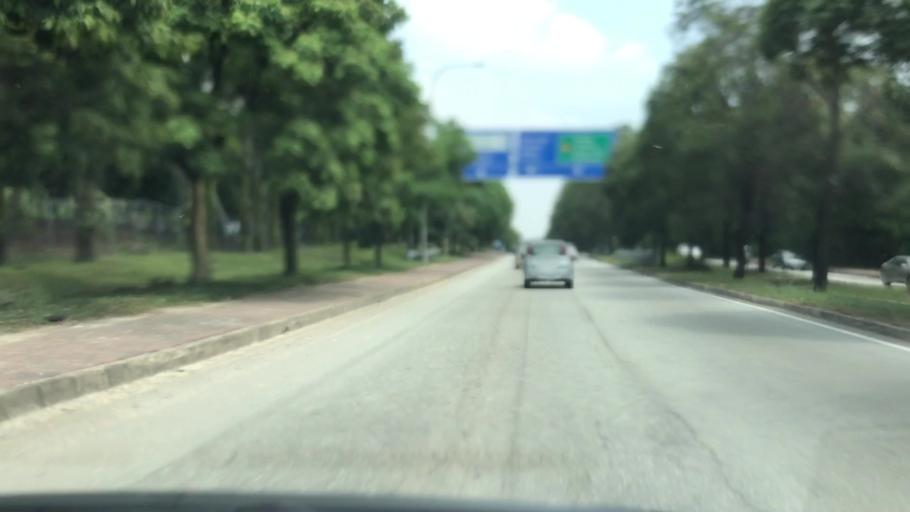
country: MY
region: Selangor
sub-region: Petaling
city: Petaling Jaya
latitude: 3.0558
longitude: 101.6628
